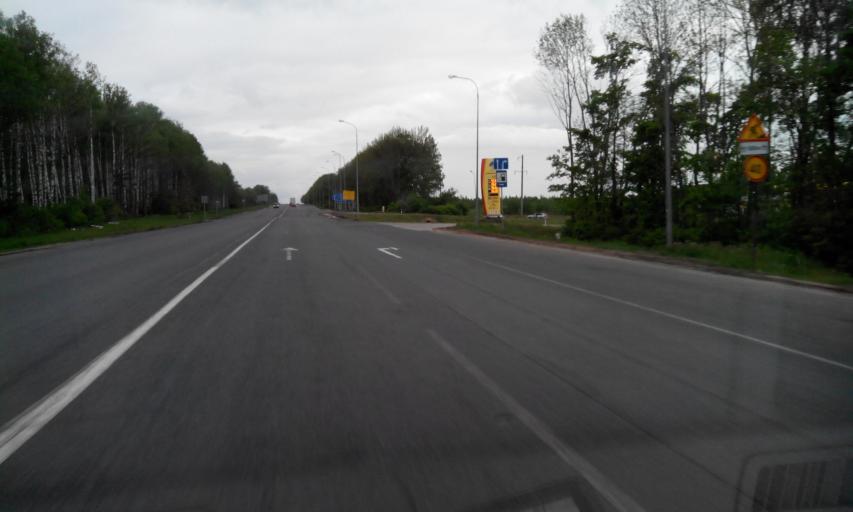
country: RU
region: Penza
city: Gorodishche
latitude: 53.2763
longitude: 45.6375
